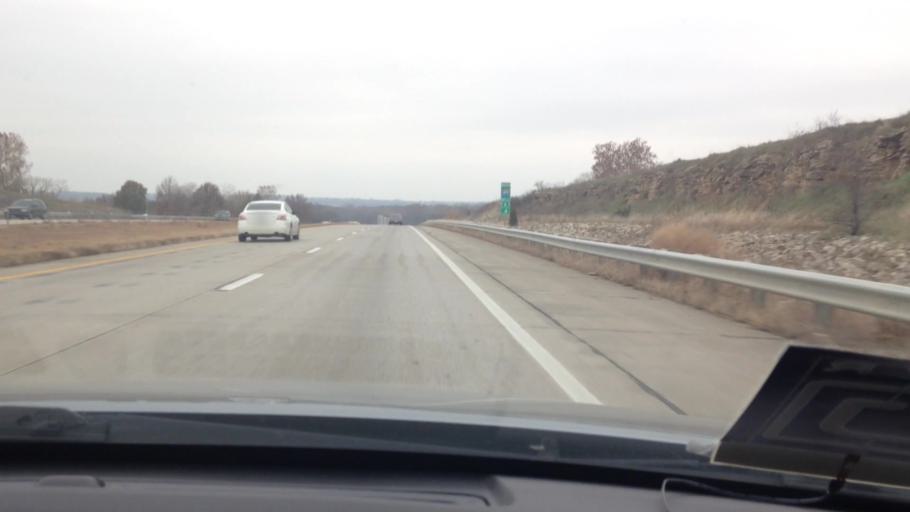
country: US
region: Missouri
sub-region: Cass County
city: Harrisonville
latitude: 38.6632
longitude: -94.3838
